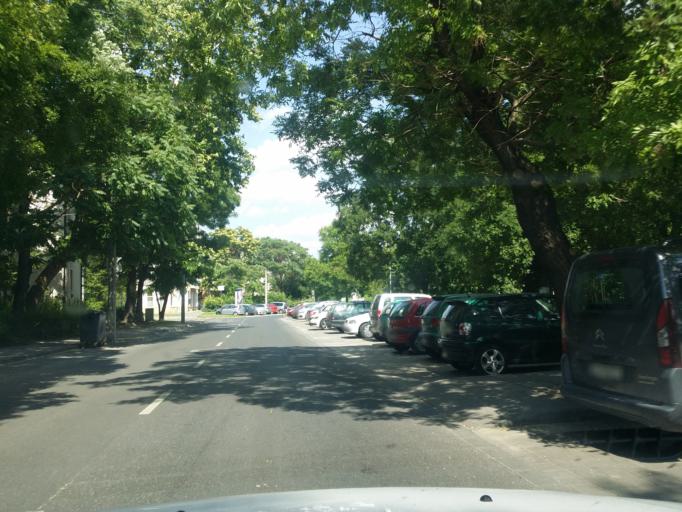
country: HU
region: Bacs-Kiskun
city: Kecskemet
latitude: 46.9036
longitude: 19.6927
